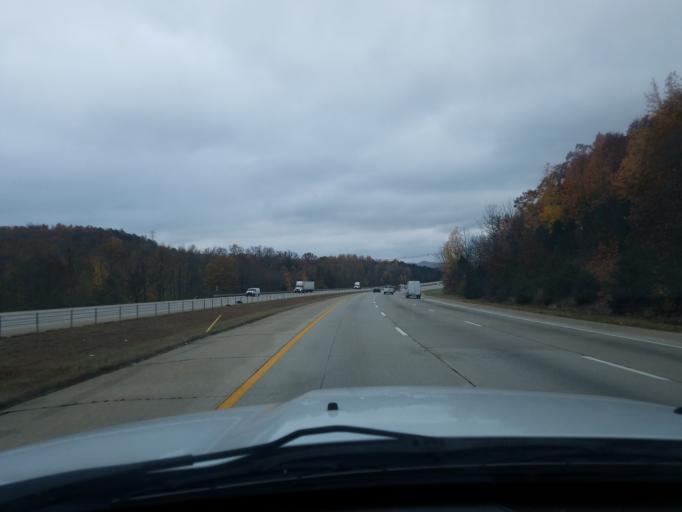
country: US
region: Kentucky
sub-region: Bullitt County
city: Shepherdsville
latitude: 37.9549
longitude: -85.6904
